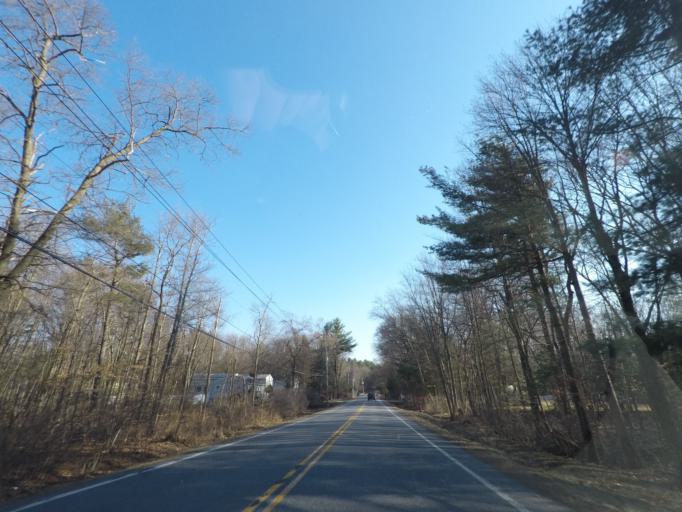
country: US
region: New York
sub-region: Saratoga County
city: Country Knolls
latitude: 42.8348
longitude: -73.7761
